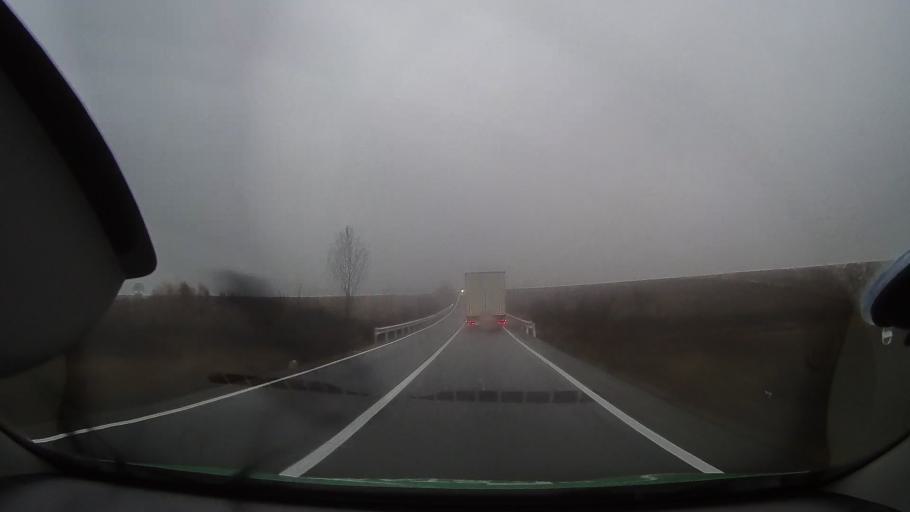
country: RO
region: Bihor
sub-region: Comuna Olcea
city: Olcea
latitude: 46.6579
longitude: 21.9611
